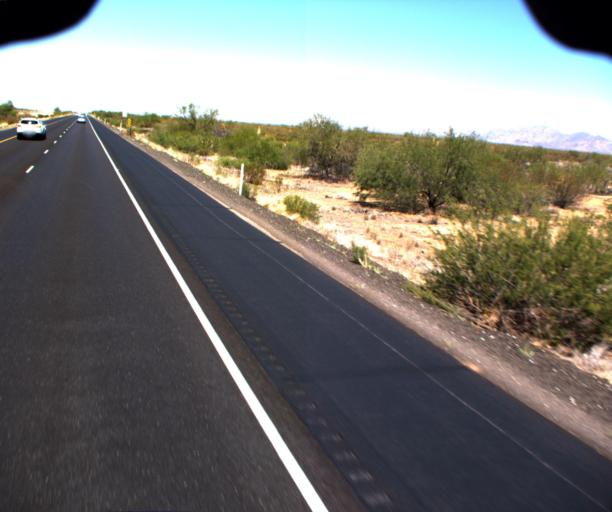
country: US
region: Arizona
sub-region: Yavapai County
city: Congress
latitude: 34.0810
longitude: -112.8895
